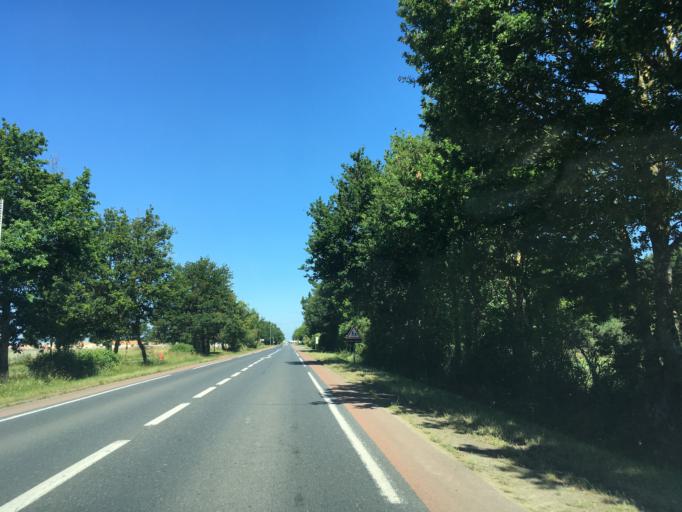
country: FR
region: Pays de la Loire
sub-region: Departement de la Vendee
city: Saint-Georges-de-Montaigu
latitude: 46.9378
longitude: -1.2780
